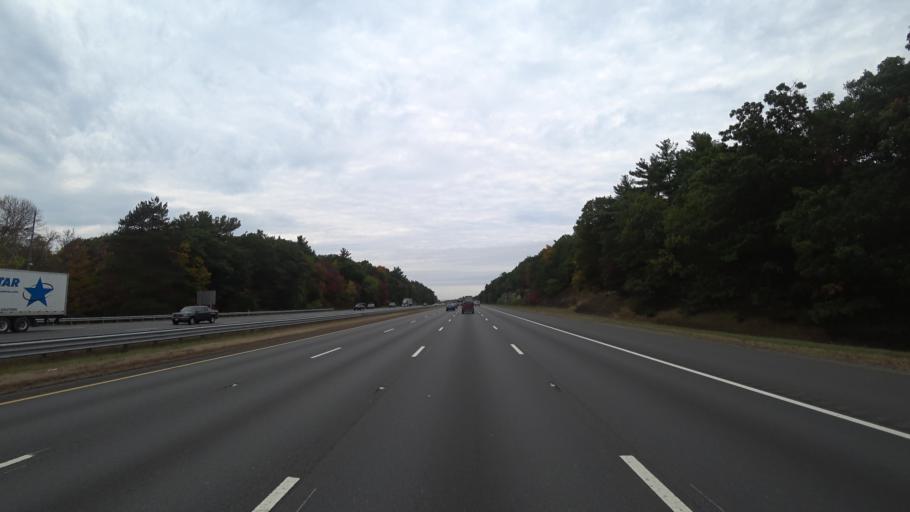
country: US
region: Massachusetts
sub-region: Middlesex County
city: Wilmington
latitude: 42.5651
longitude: -71.1442
